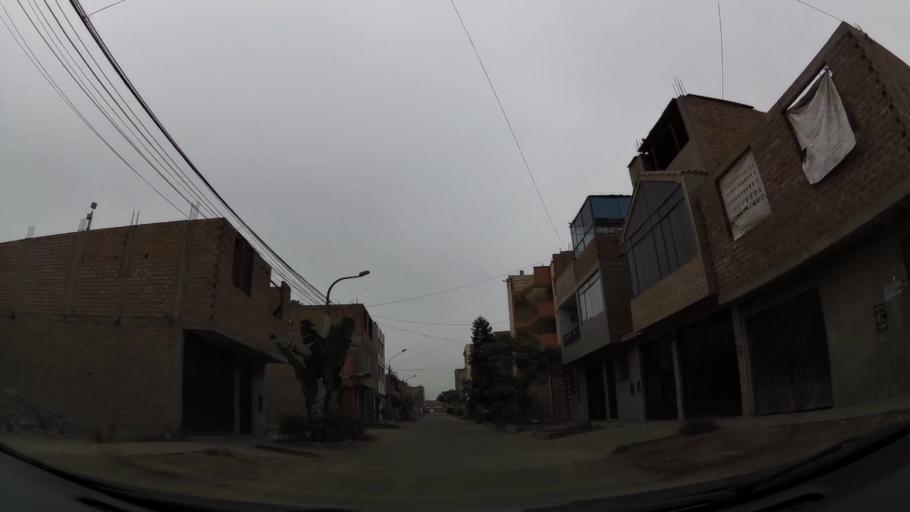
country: PE
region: Lima
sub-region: Lima
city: Urb. Santo Domingo
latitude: -11.8873
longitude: -77.0414
